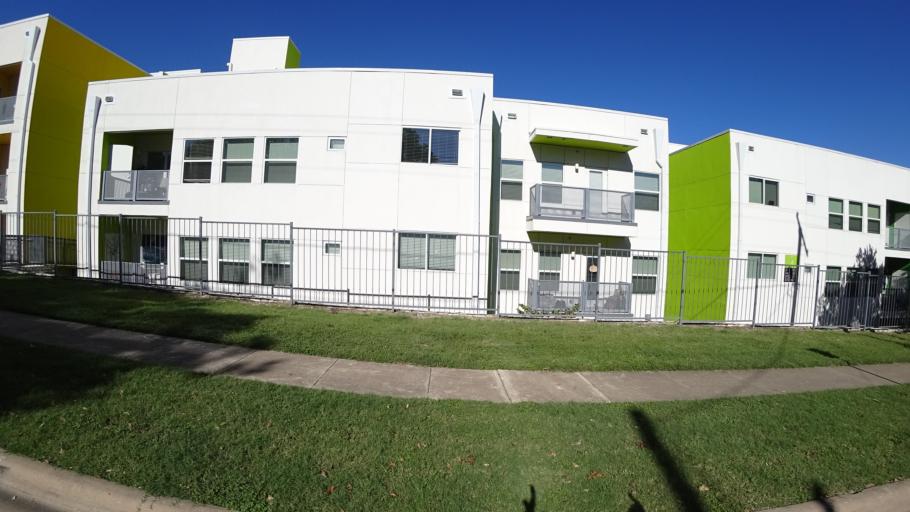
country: US
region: Texas
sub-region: Travis County
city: Austin
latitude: 30.2423
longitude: -97.7560
